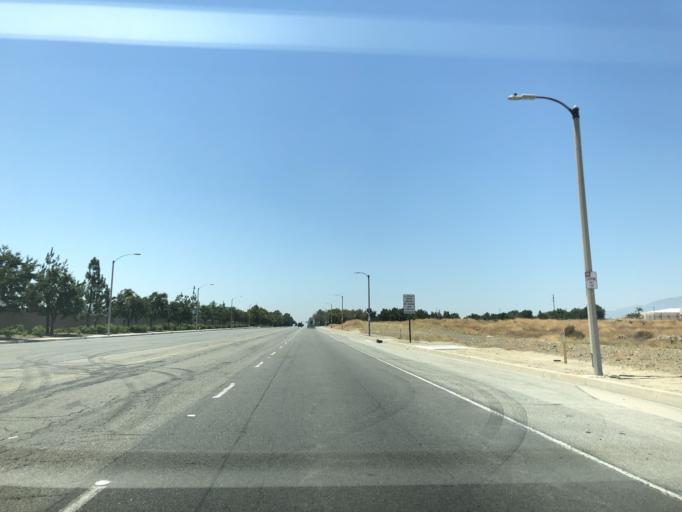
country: US
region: California
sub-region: San Bernardino County
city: Rancho Cucamonga
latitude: 34.0773
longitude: -117.5251
